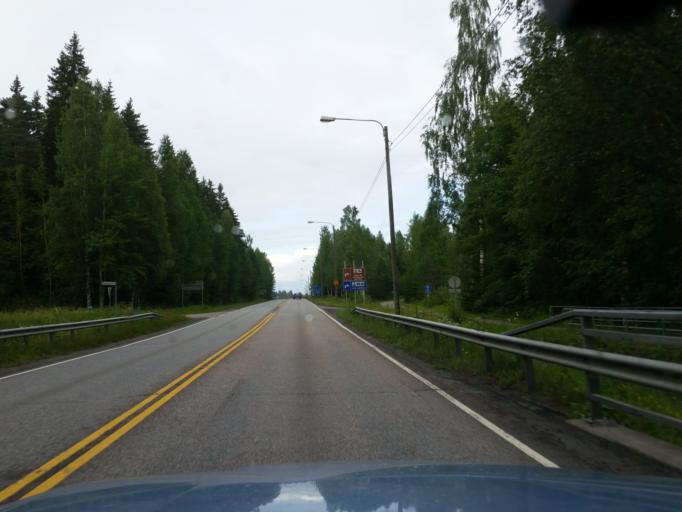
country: FI
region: Southern Savonia
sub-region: Pieksaemaeki
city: Juva
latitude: 61.8904
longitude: 27.7972
